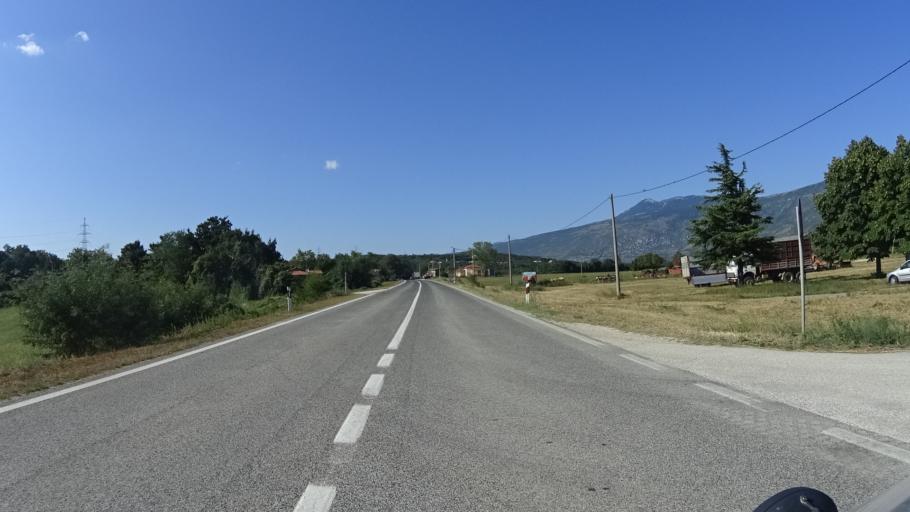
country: HR
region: Istarska
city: Vinez
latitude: 45.1960
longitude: 14.1335
